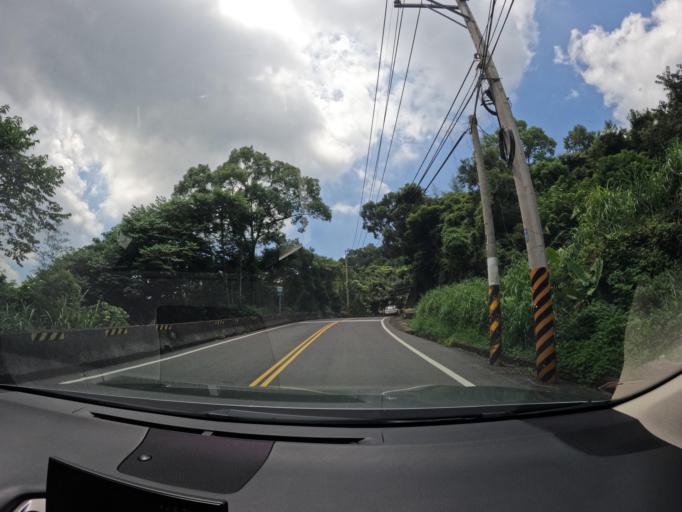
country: TW
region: Taiwan
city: Fengyuan
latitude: 24.3862
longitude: 120.8134
